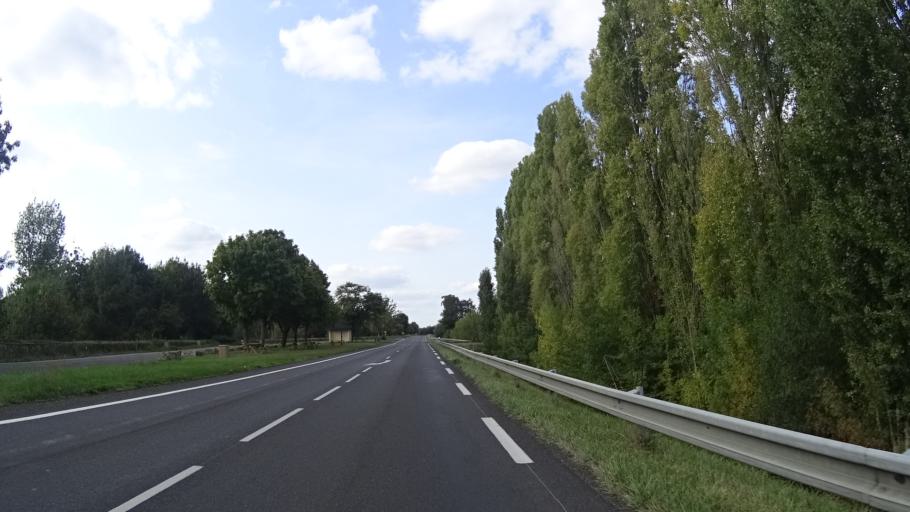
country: FR
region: Pays de la Loire
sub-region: Departement de Maine-et-Loire
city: Gennes
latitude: 47.3601
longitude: -0.2461
